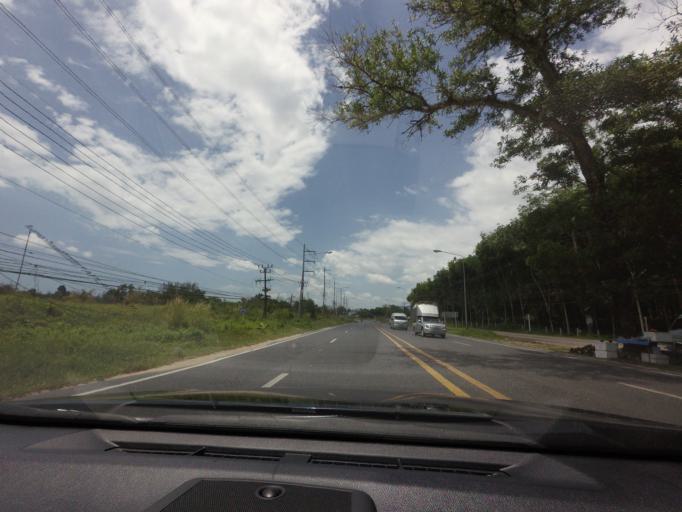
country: TH
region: Phangnga
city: Ban Khao Lak
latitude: 8.6518
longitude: 98.2530
